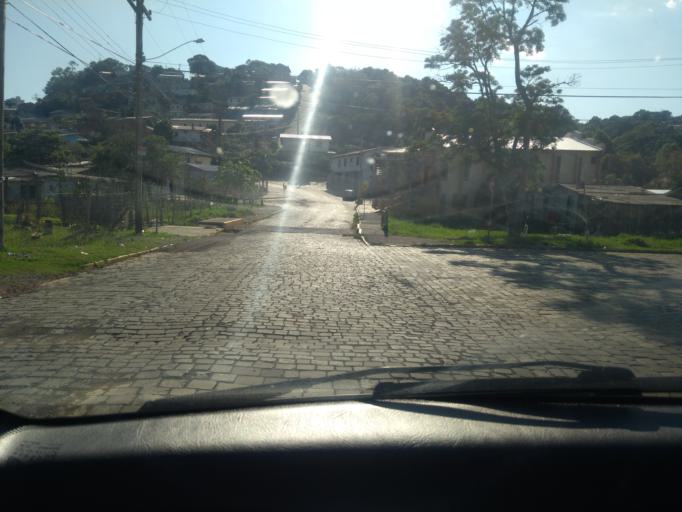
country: BR
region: Rio Grande do Sul
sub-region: Veranopolis
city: Veranopolis
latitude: -28.9394
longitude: -51.5610
